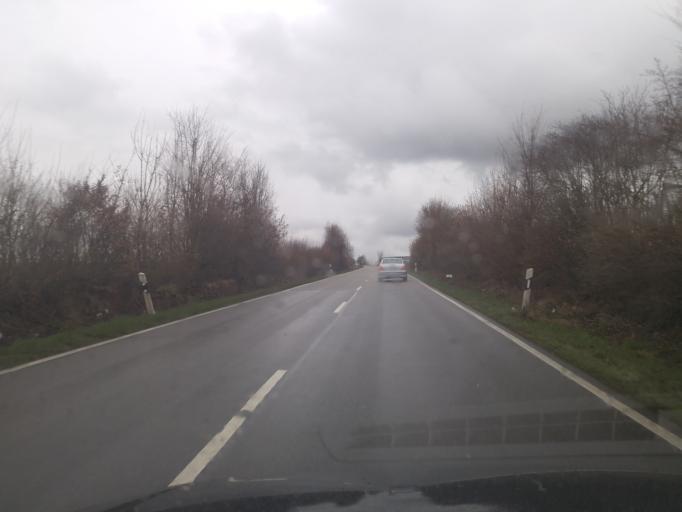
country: DE
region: Baden-Wuerttemberg
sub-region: Regierungsbezirk Stuttgart
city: Affalterbach
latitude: 48.9318
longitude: 9.3141
